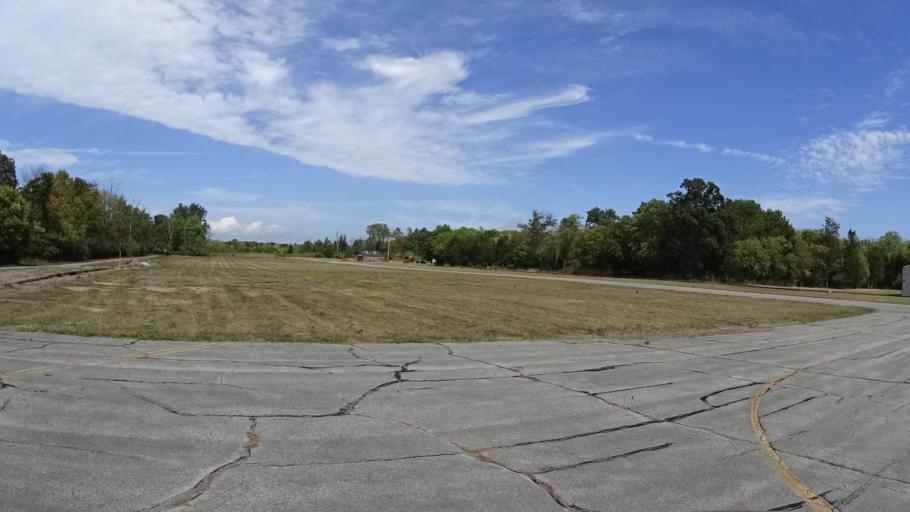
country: US
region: Ohio
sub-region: Erie County
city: Sandusky
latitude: 41.6037
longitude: -82.6876
